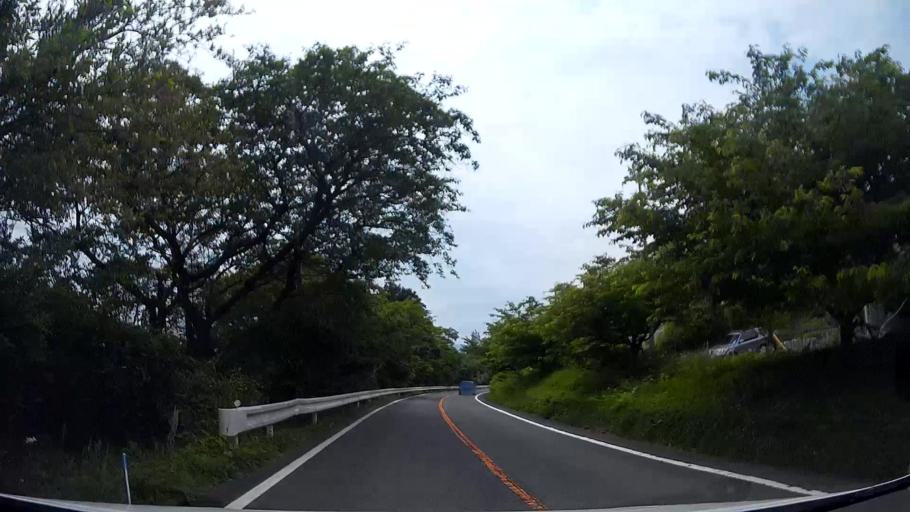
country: JP
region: Shizuoka
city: Ito
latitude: 34.9009
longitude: 139.1053
